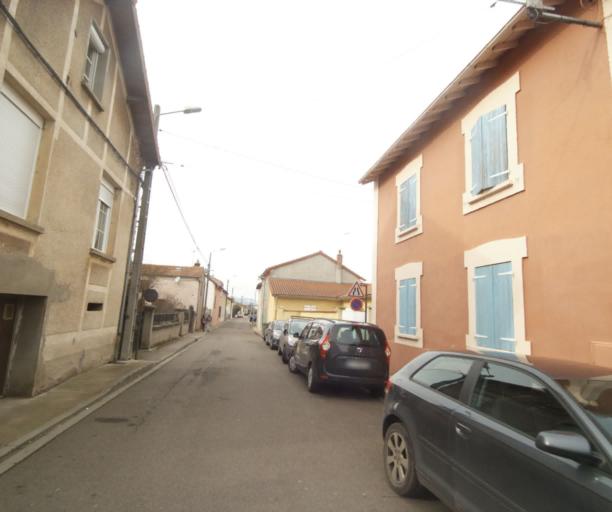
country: FR
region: Rhone-Alpes
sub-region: Departement de la Loire
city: Roanne
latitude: 46.0263
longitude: 4.0589
